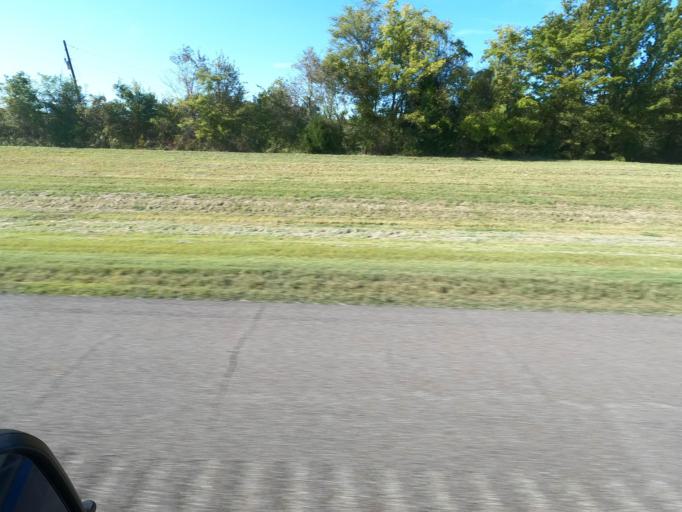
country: US
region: Tennessee
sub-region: Dyer County
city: Dyersburg
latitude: 36.0749
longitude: -89.3454
